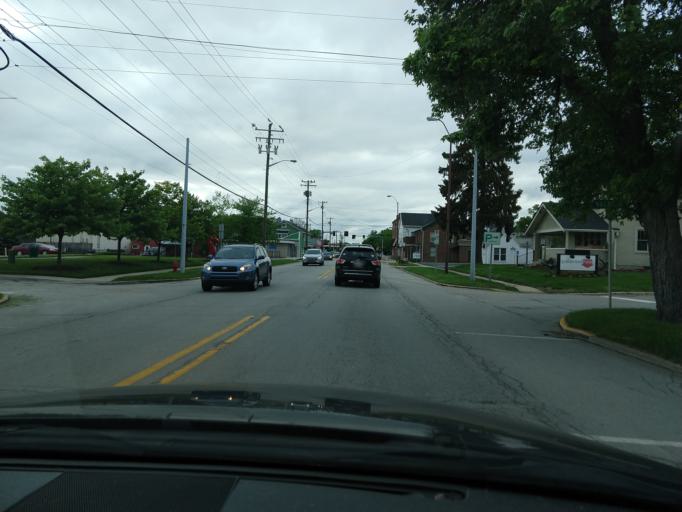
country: US
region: Indiana
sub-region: Hamilton County
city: Westfield
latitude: 40.0428
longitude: -86.1261
